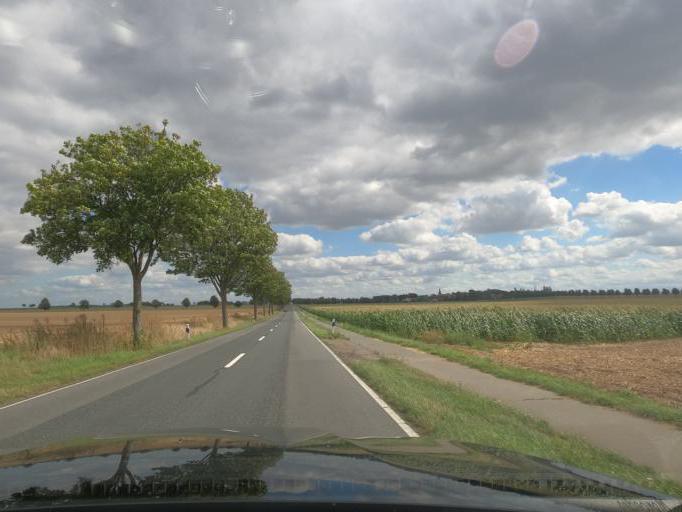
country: DE
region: Lower Saxony
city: Hohenhameln
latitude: 52.2504
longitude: 10.0998
